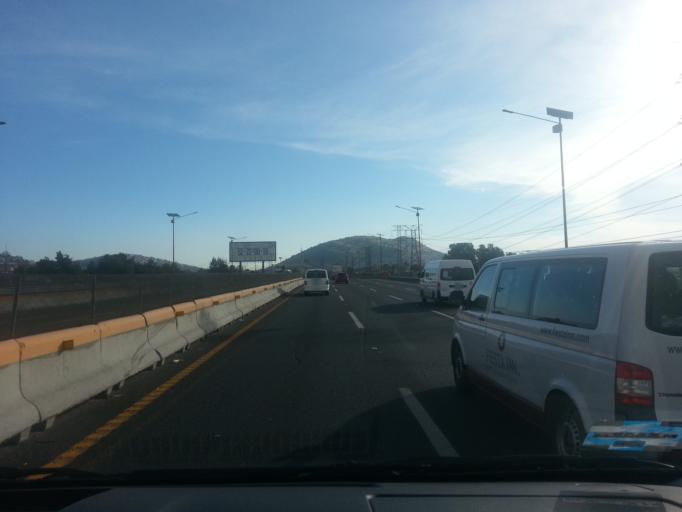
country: MX
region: Mexico
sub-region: Tlalnepantla de Baz
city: Puerto Escondido (Tepeolulco Puerto Escondido)
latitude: 19.5306
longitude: -99.0809
